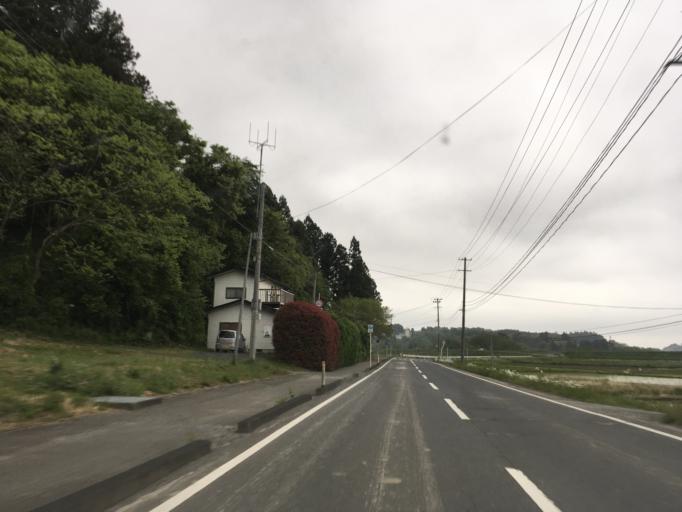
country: JP
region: Miyagi
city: Wakuya
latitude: 38.7224
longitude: 141.2958
